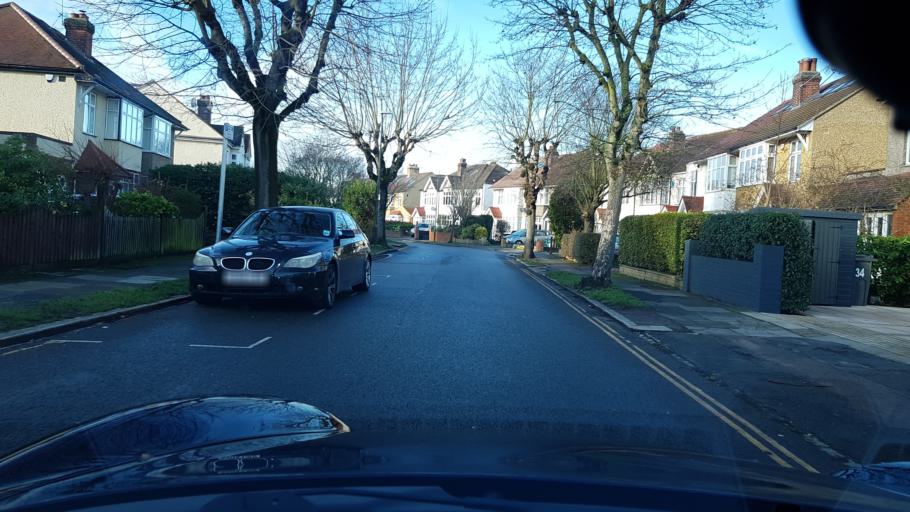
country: GB
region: England
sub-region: Greater London
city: Morden
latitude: 51.4046
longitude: -0.2020
